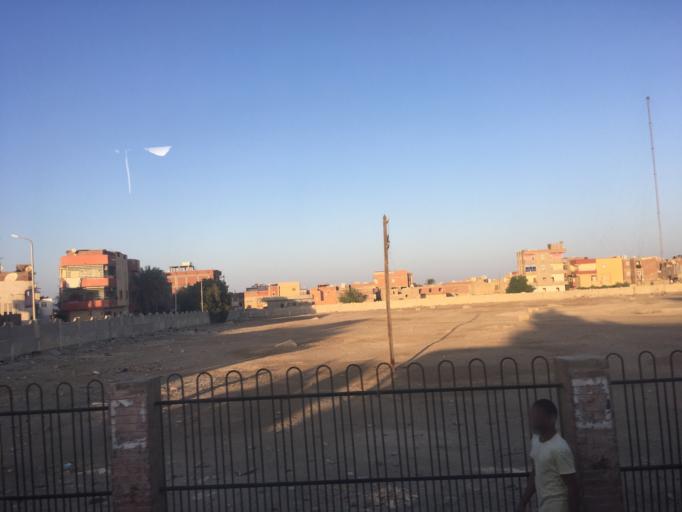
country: EG
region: Red Sea
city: Al Qusayr
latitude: 26.1116
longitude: 34.2782
